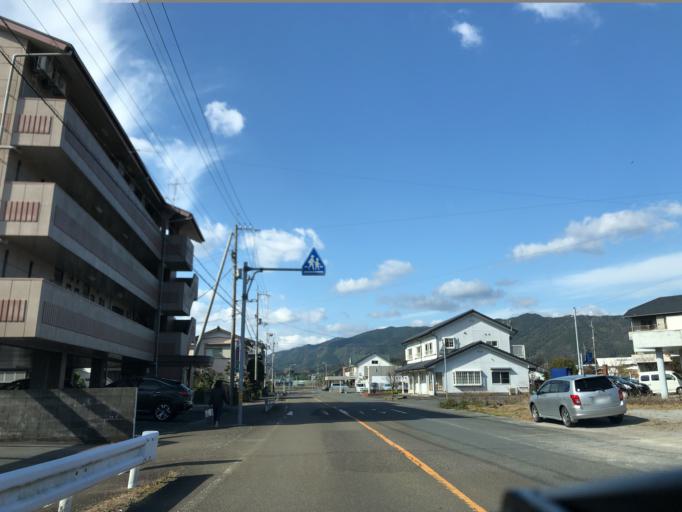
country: JP
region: Kochi
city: Sukumo
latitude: 32.9264
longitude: 132.7014
